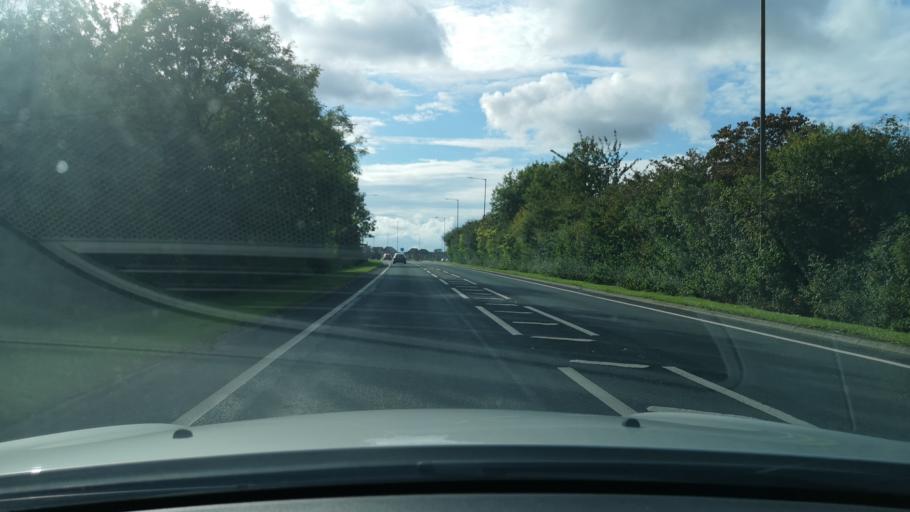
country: GB
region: England
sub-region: East Riding of Yorkshire
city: Leconfield
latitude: 53.8571
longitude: -0.4453
